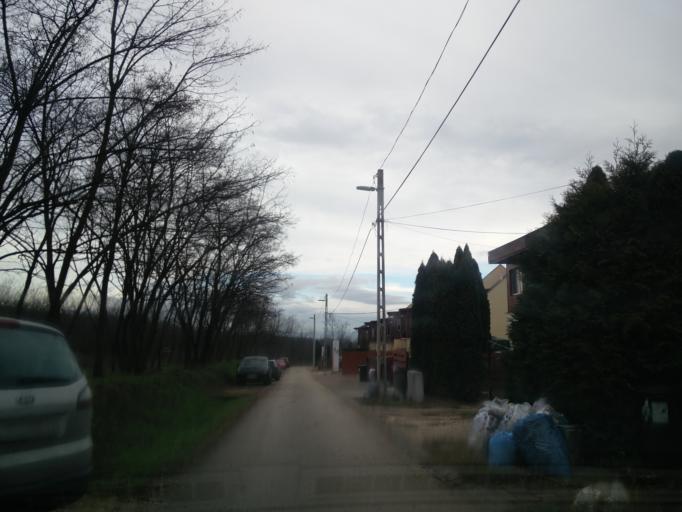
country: HU
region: Pest
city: Fot
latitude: 47.6576
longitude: 19.2231
